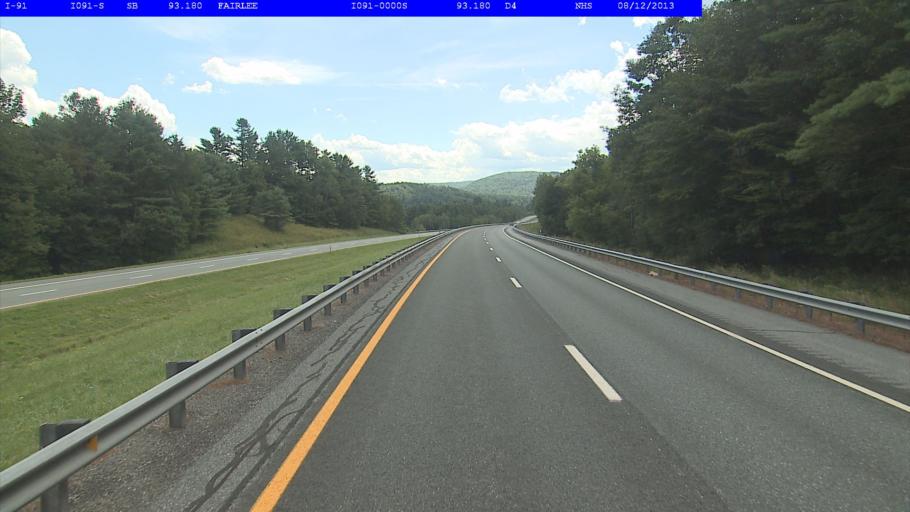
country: US
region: New Hampshire
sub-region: Grafton County
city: Orford
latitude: 43.9215
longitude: -72.1330
